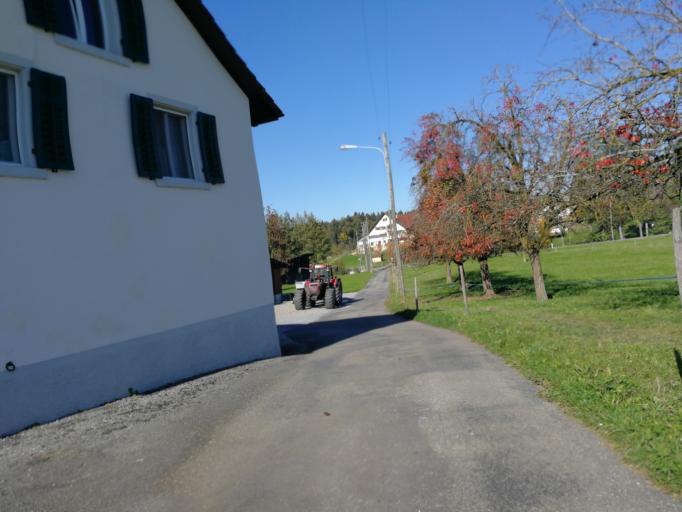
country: CH
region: Zurich
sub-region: Bezirk Meilen
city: Hombrechtikon
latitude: 47.2624
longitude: 8.7611
